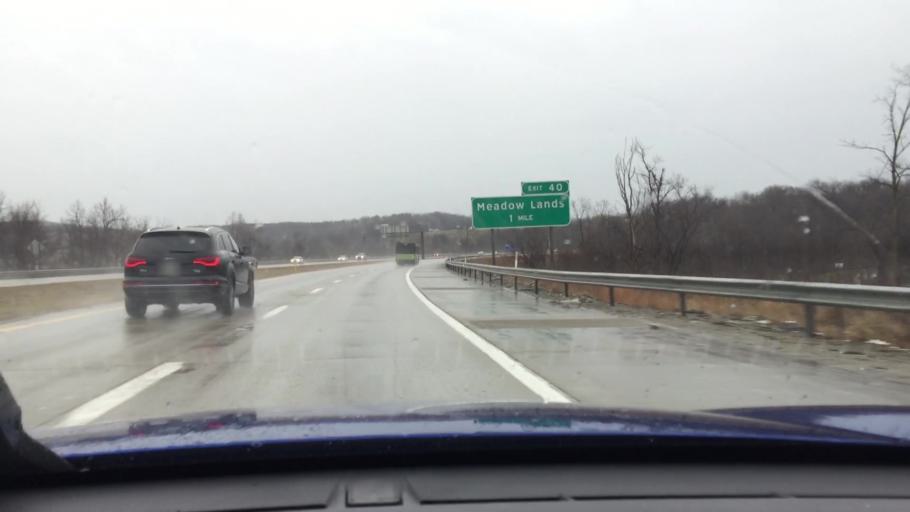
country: US
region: Pennsylvania
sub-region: Washington County
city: Washington
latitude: 40.2054
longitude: -80.2480
